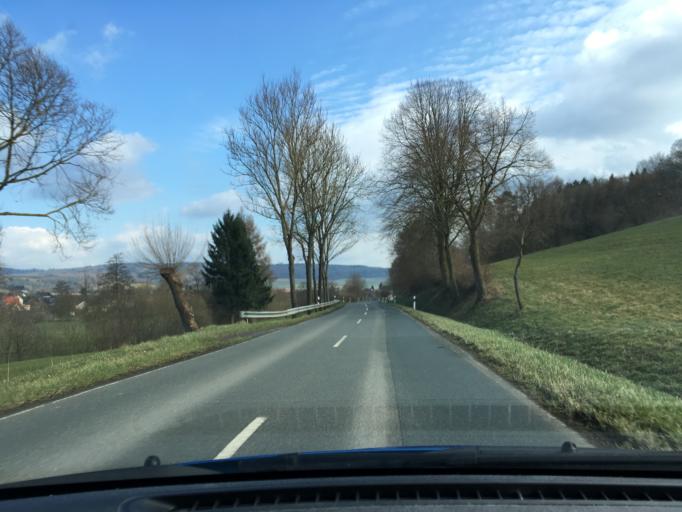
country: DE
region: Lower Saxony
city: Uslar
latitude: 51.6356
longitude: 9.6497
